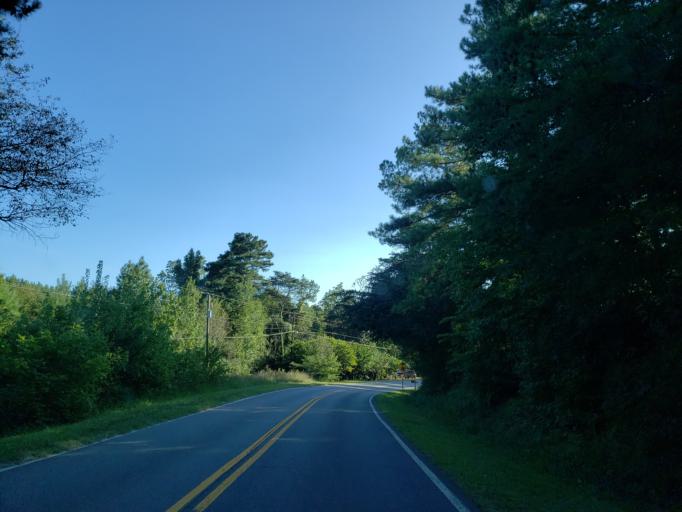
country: US
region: Georgia
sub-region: Bartow County
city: Rydal
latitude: 34.2806
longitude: -84.8093
